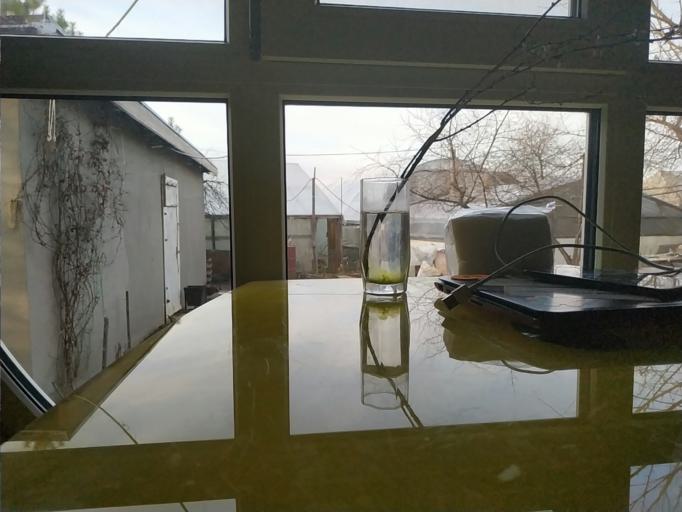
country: RU
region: Republic of Karelia
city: Suoyarvi
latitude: 62.0812
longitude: 32.1725
